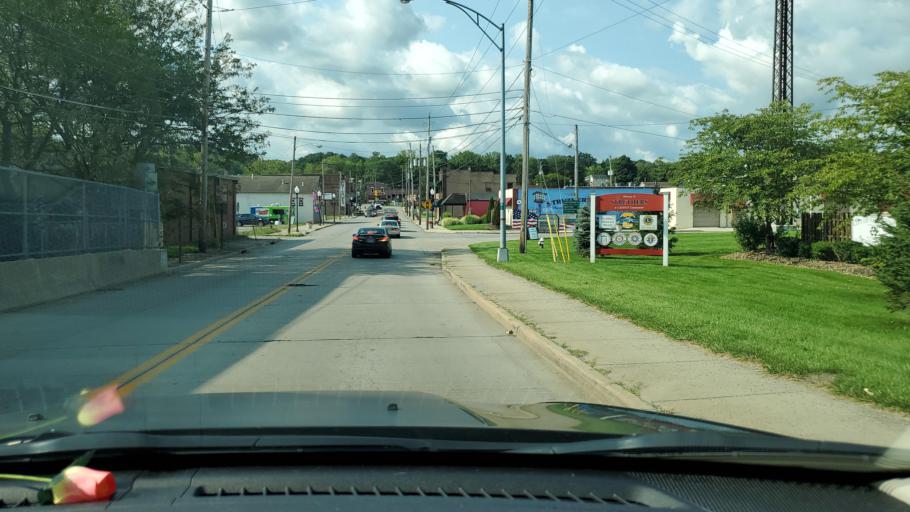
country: US
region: Ohio
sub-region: Mahoning County
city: Struthers
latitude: 41.0578
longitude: -80.5862
